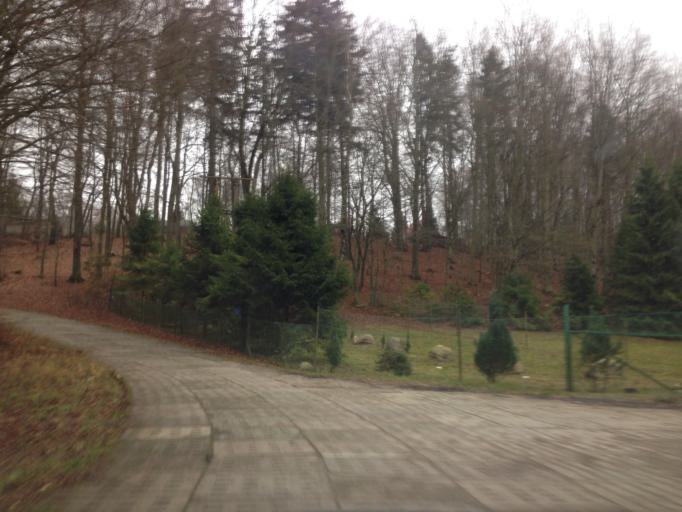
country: PL
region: Pomeranian Voivodeship
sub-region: Powiat gdanski
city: Przywidz
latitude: 54.1847
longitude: 18.3431
